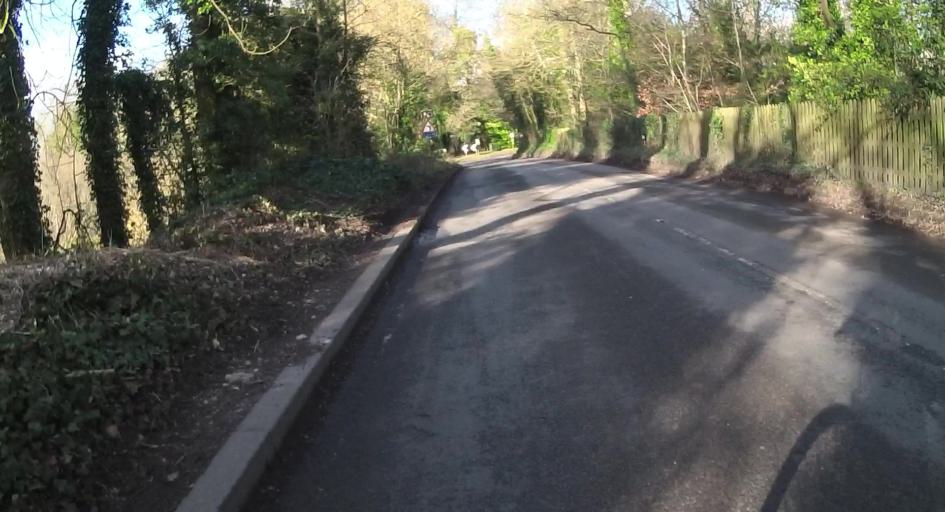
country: GB
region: England
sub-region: Hampshire
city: Four Marks
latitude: 51.0957
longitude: -1.1609
